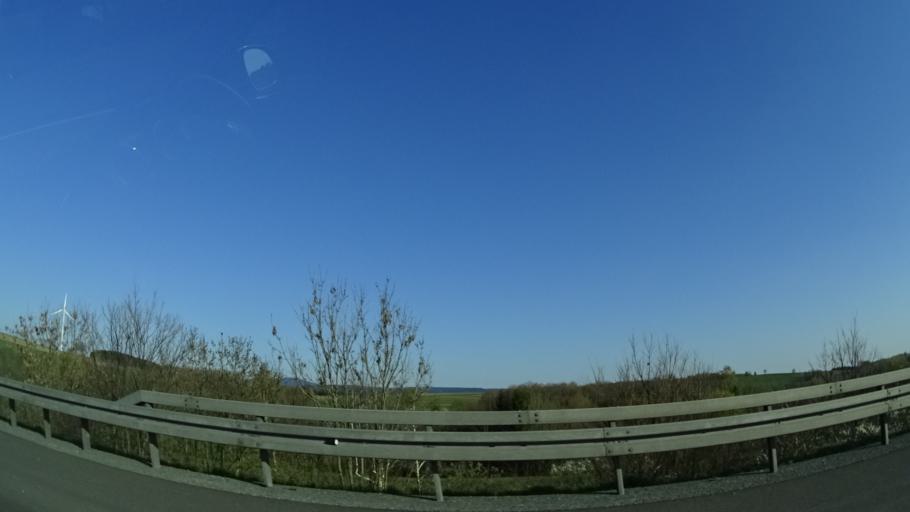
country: DE
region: Bavaria
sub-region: Upper Franconia
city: Marktschorgast
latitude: 50.0843
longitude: 11.6727
